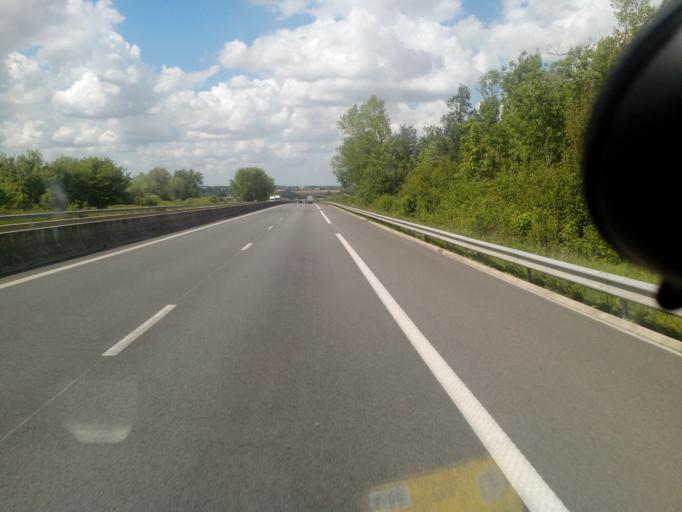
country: FR
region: Nord-Pas-de-Calais
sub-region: Departement du Nord
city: Godewaersvelde
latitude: 50.7837
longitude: 2.6251
